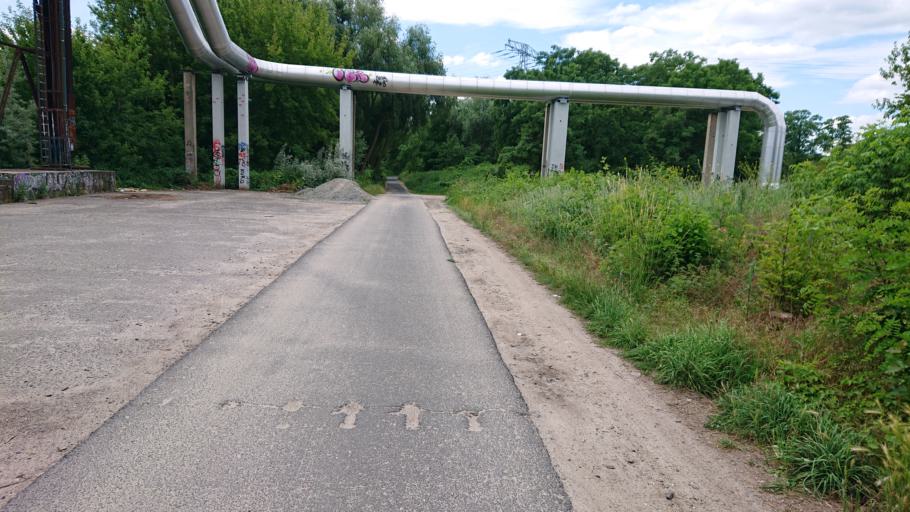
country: DE
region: Brandenburg
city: Potsdam
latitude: 52.3727
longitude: 13.1118
